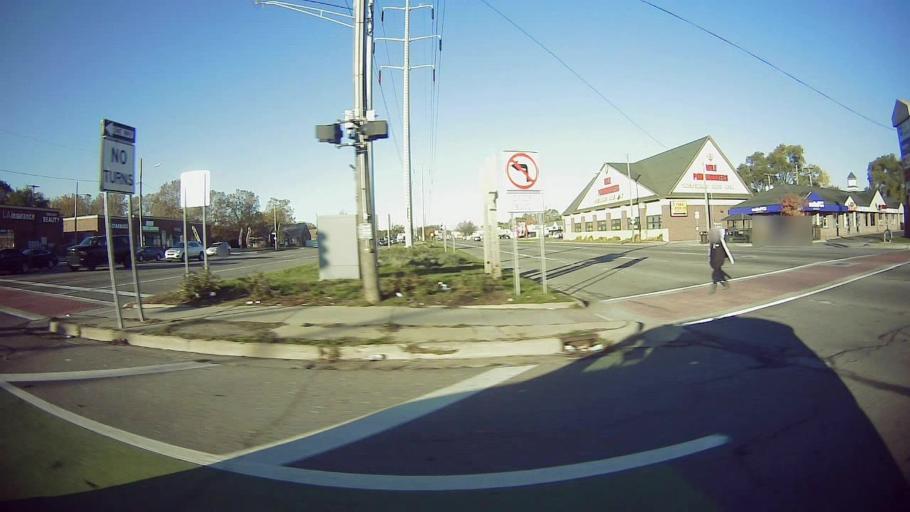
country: US
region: Michigan
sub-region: Macomb County
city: Warren
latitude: 42.4459
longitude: -83.0248
